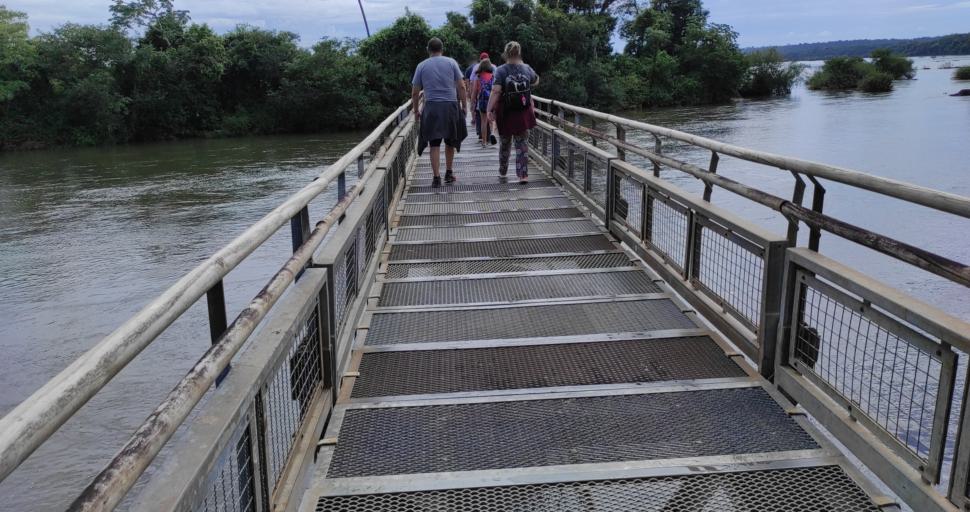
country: AR
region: Misiones
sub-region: Departamento de Iguazu
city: Puerto Iguazu
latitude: -25.6987
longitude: -54.4415
